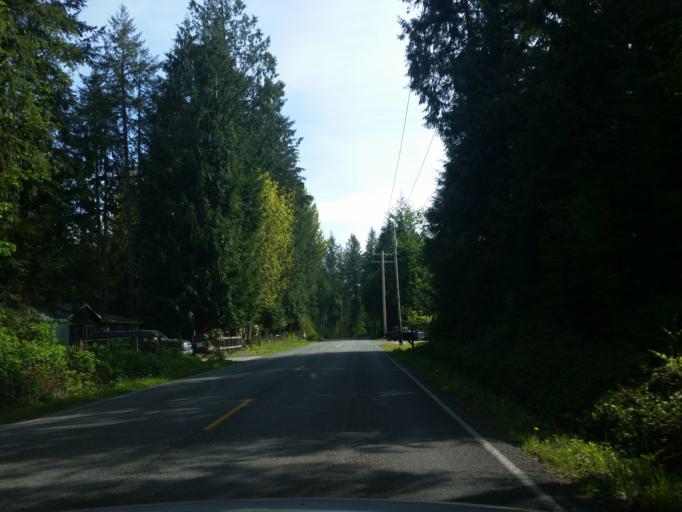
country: US
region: Washington
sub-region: Snohomish County
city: Granite Falls
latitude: 48.0308
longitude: -121.9152
